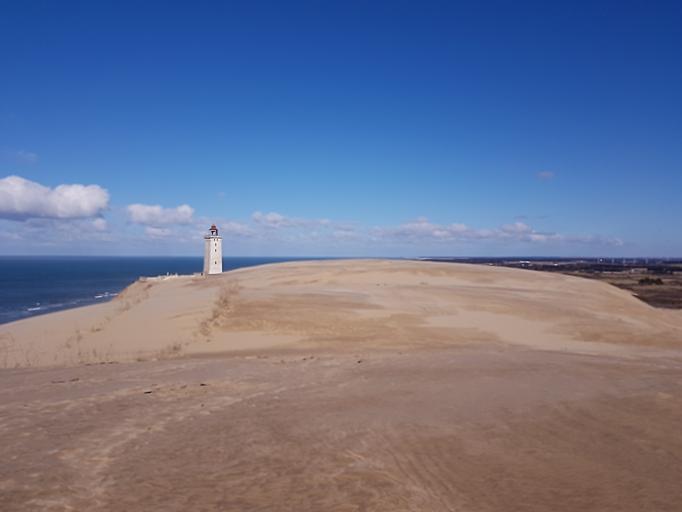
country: DK
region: North Denmark
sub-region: Hjorring Kommune
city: Vra
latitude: 57.4467
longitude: 9.7736
